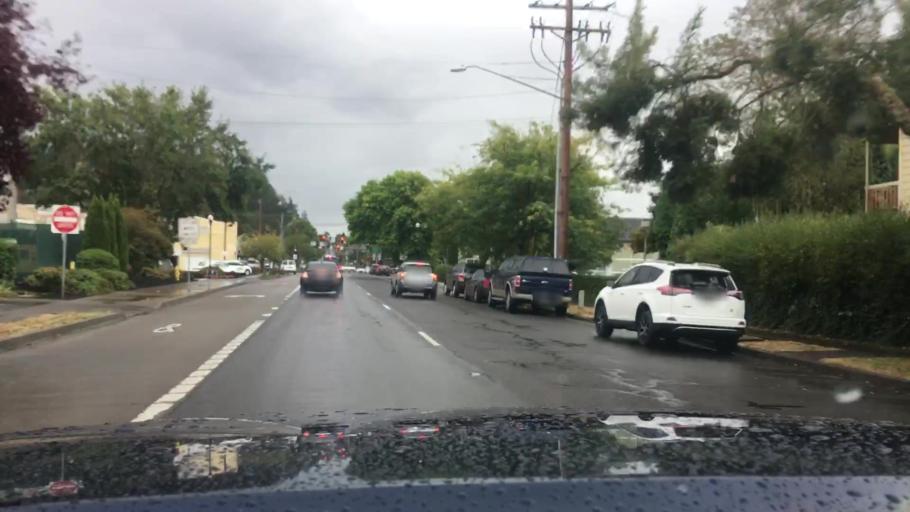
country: US
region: Oregon
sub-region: Lane County
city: Springfield
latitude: 44.0477
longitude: -123.0233
